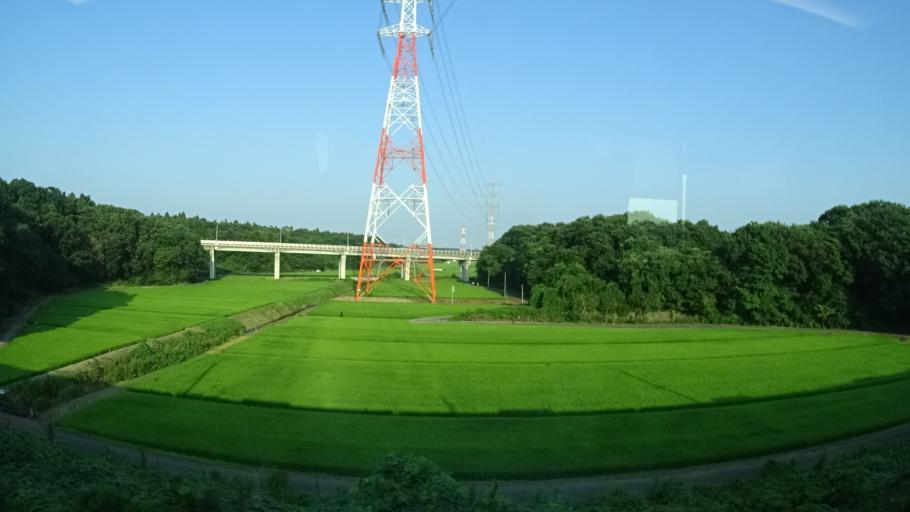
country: JP
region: Ibaraki
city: Funaishikawa
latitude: 36.4432
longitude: 140.5457
